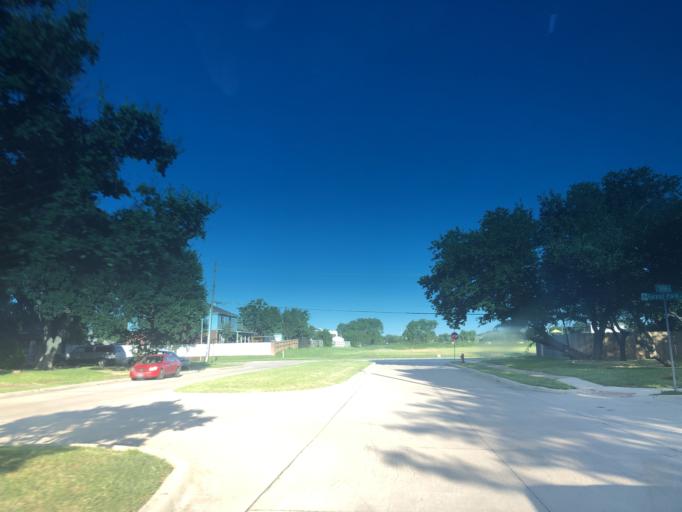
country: US
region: Texas
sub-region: Dallas County
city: Grand Prairie
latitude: 32.7019
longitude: -97.0147
